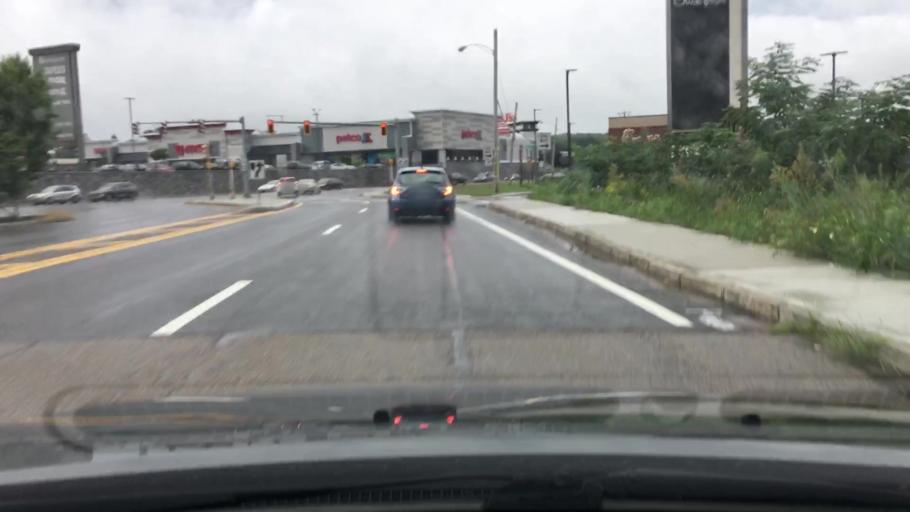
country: US
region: Rhode Island
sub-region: Providence County
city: Valley Falls
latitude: 41.9212
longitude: -71.3573
